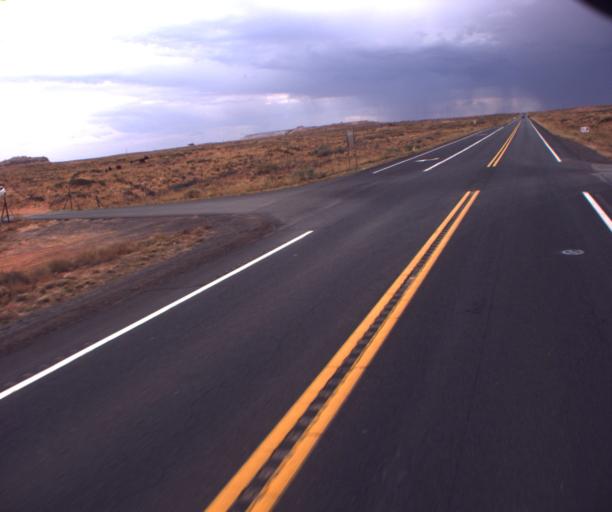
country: US
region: Arizona
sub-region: Coconino County
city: Kaibito
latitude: 36.3062
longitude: -110.9681
